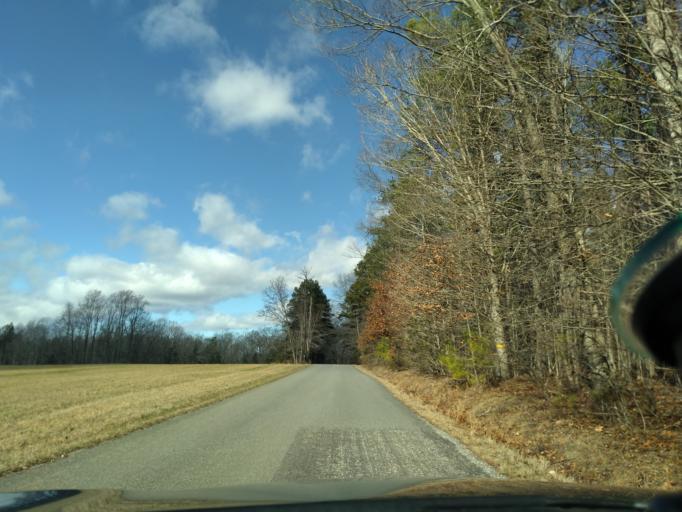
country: US
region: Virginia
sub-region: Nottoway County
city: Crewe
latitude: 37.1747
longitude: -78.2626
